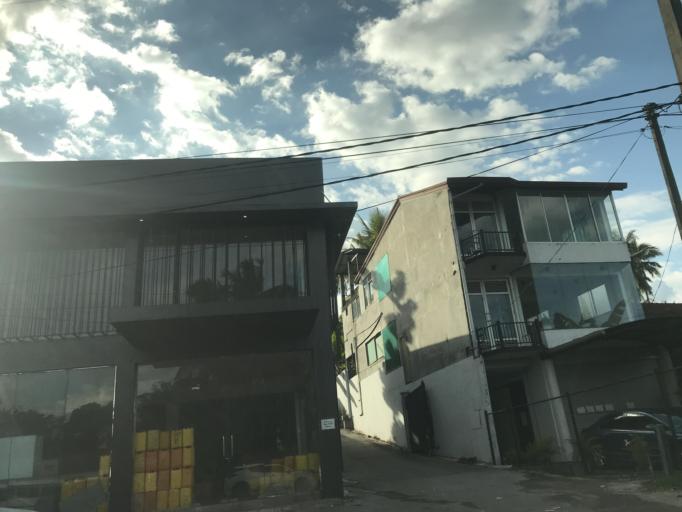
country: LK
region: Western
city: Gampaha
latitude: 7.0445
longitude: 79.9965
